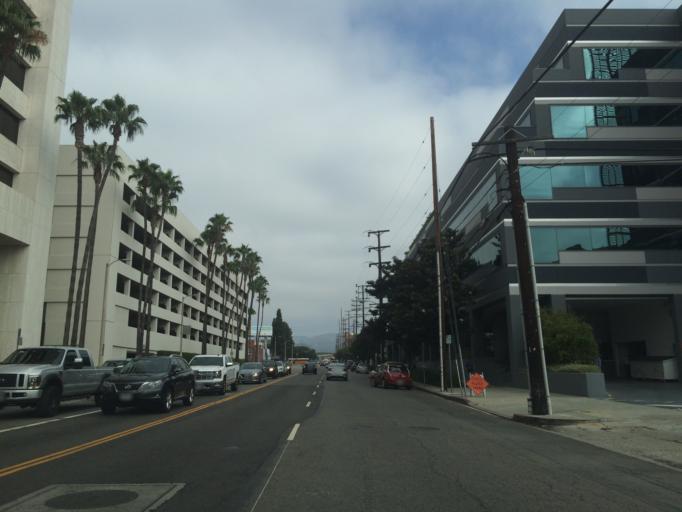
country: US
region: California
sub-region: Los Angeles County
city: Westwood, Los Angeles
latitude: 34.0479
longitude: -118.4445
